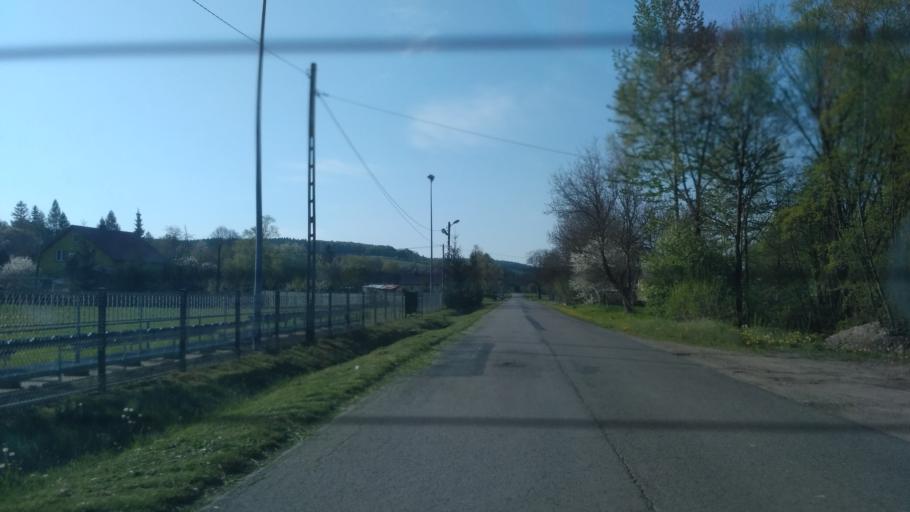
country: PL
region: Subcarpathian Voivodeship
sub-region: Powiat jaroslawski
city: Pruchnik
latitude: 49.8815
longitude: 22.5625
